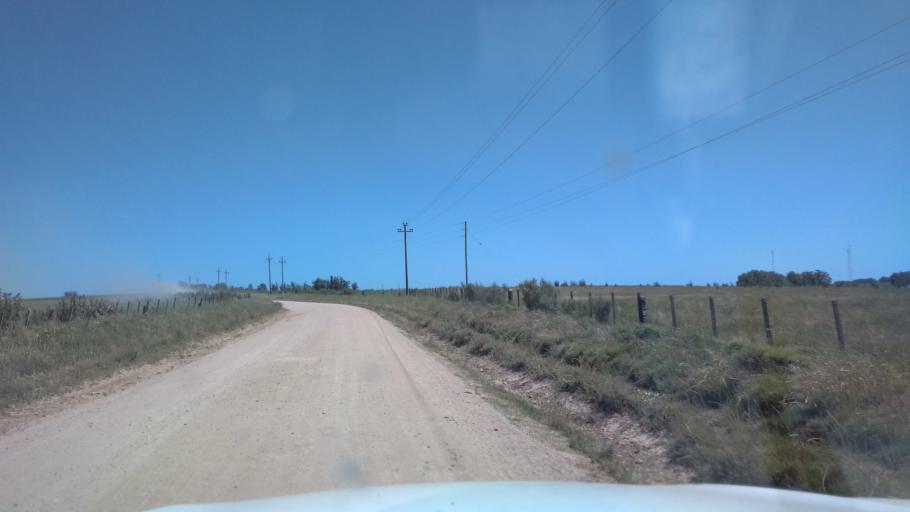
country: UY
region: Florida
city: Casupa
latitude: -34.0537
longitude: -55.8931
